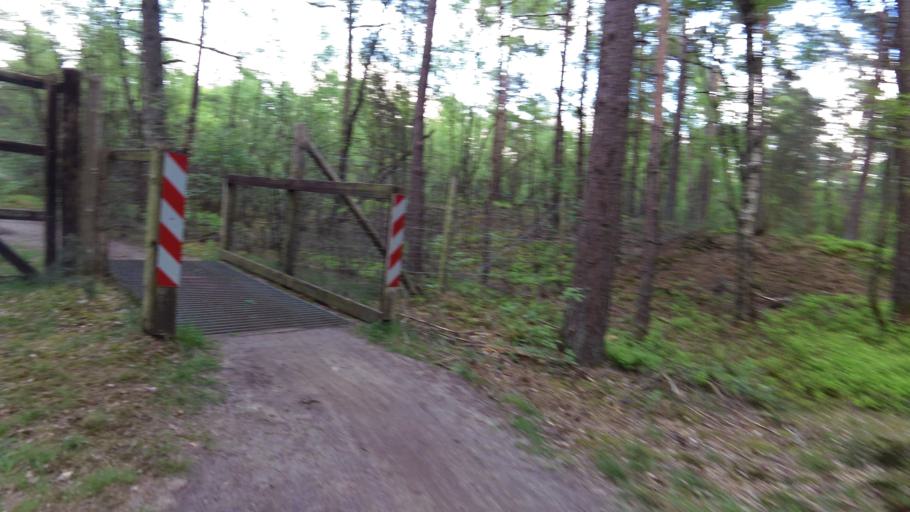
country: NL
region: Gelderland
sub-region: Gemeente Brummen
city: Eerbeek
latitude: 52.0843
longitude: 6.0517
